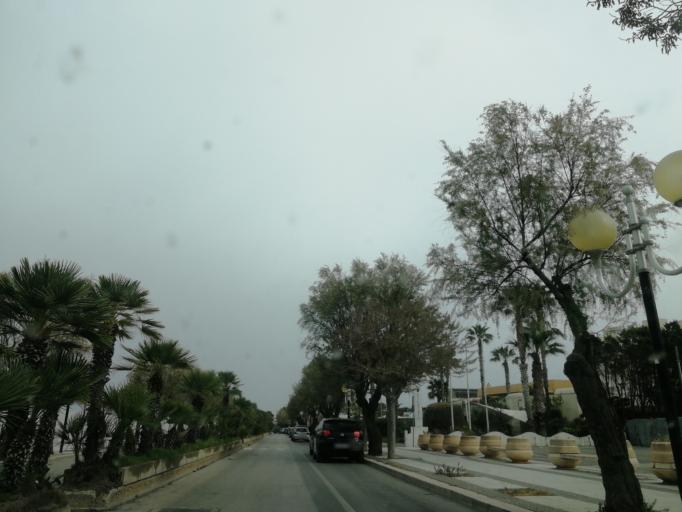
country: IT
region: Apulia
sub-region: Provincia di Barletta - Andria - Trani
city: Barletta
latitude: 41.3212
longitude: 16.2950
